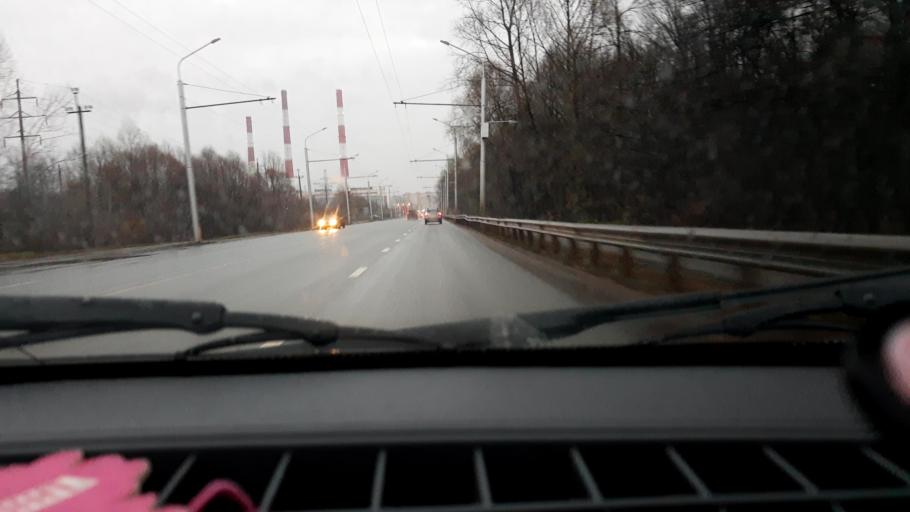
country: RU
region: Bashkortostan
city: Ufa
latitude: 54.7898
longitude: 56.1027
